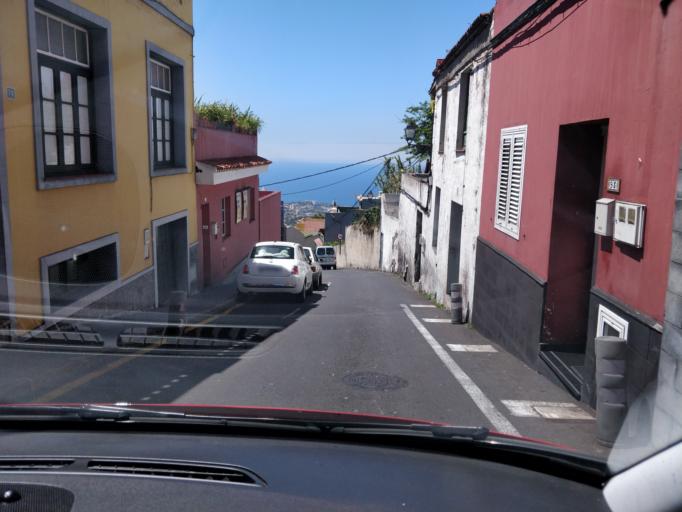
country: ES
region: Canary Islands
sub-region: Provincia de Santa Cruz de Tenerife
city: La Orotava
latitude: 28.3852
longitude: -16.5220
